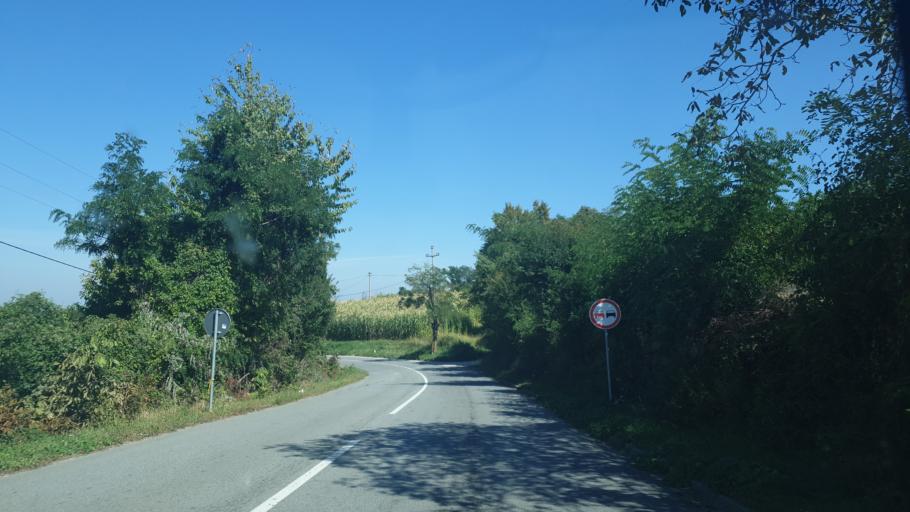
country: RS
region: Central Serbia
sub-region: Kolubarski Okrug
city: Mionica
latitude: 44.1780
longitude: 20.0367
